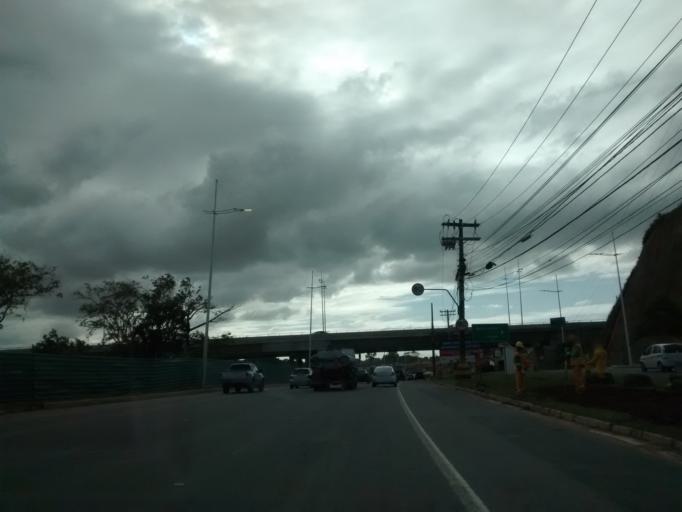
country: BR
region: Bahia
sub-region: Lauro De Freitas
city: Lauro de Freitas
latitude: -12.9267
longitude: -38.3833
